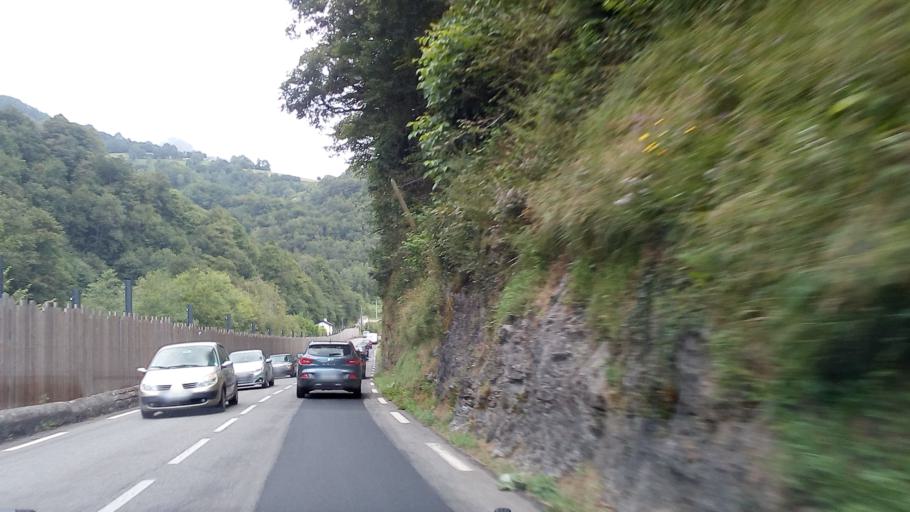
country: FR
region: Aquitaine
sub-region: Departement des Pyrenees-Atlantiques
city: Arette
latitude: 43.0321
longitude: -0.6048
